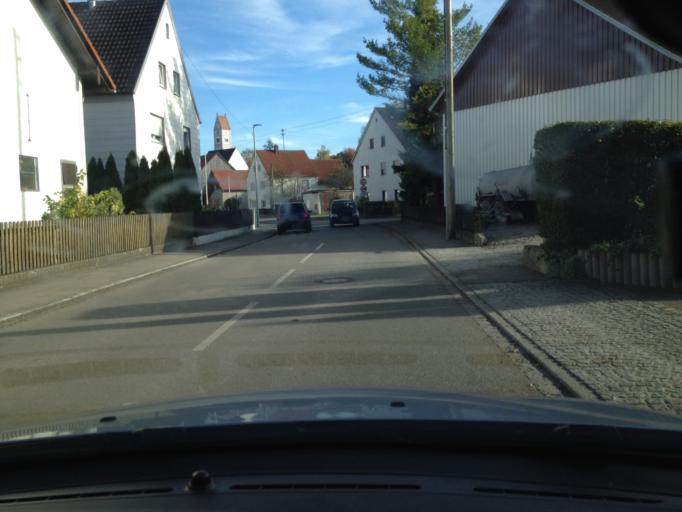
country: DE
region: Bavaria
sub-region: Swabia
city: Wehringen
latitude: 48.2476
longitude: 10.7985
